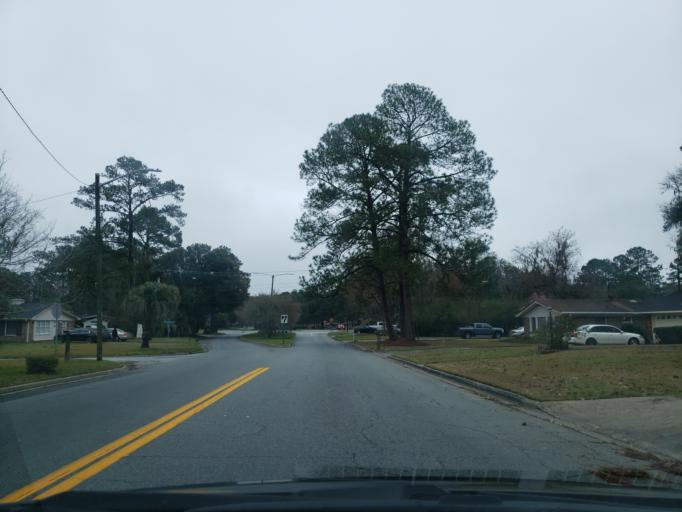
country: US
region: Georgia
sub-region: Chatham County
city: Montgomery
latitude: 31.9723
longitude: -81.1533
